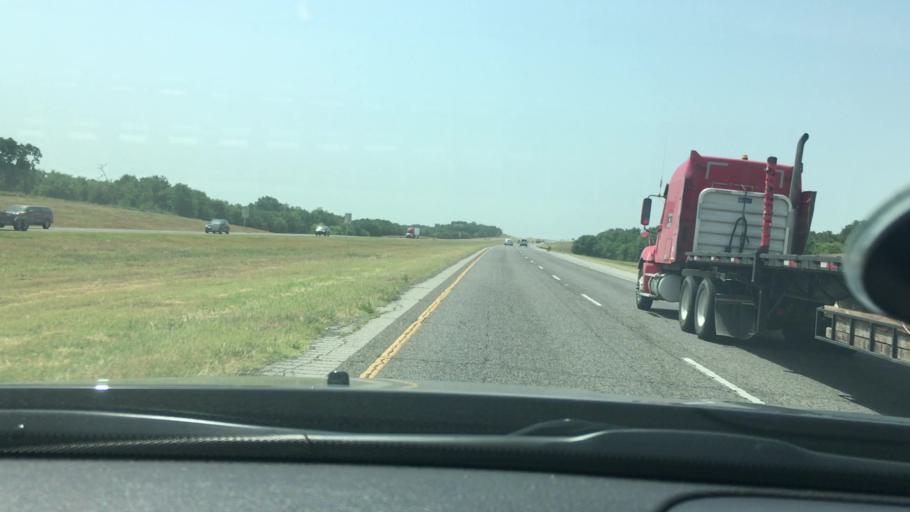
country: US
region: Oklahoma
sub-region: Garvin County
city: Wynnewood
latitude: 34.5878
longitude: -97.2049
